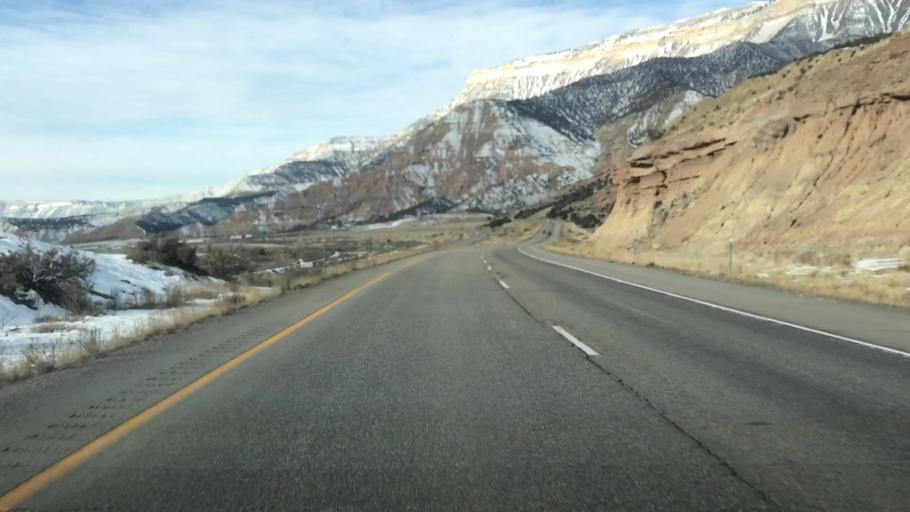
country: US
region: Colorado
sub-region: Garfield County
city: Battlement Mesa
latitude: 39.4993
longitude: -107.9218
